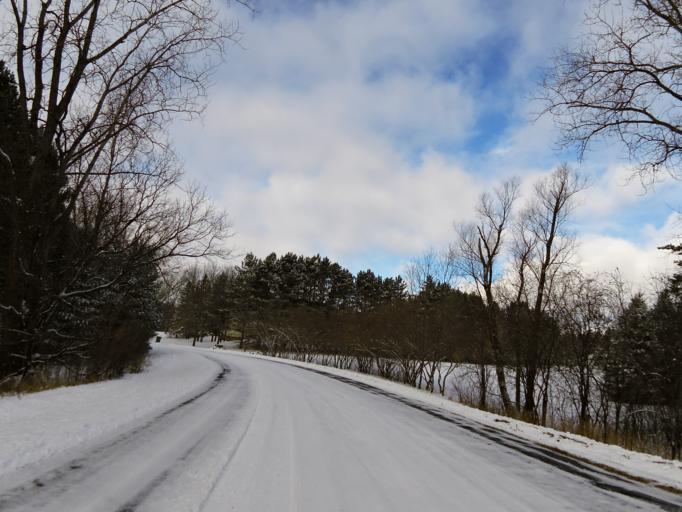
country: US
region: Minnesota
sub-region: Washington County
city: Lake Elmo
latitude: 44.9763
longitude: -92.8329
